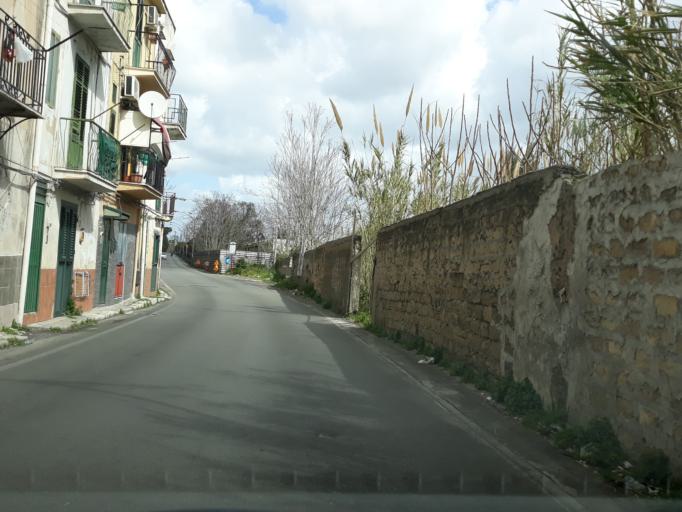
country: IT
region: Sicily
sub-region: Palermo
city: Monreale
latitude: 38.0960
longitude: 13.3097
